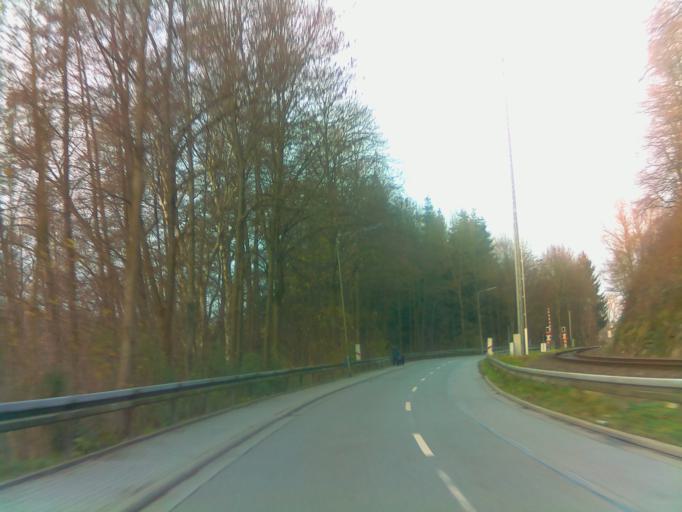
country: DE
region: Hesse
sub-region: Regierungsbezirk Darmstadt
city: Birkenau
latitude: 49.5690
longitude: 8.7122
